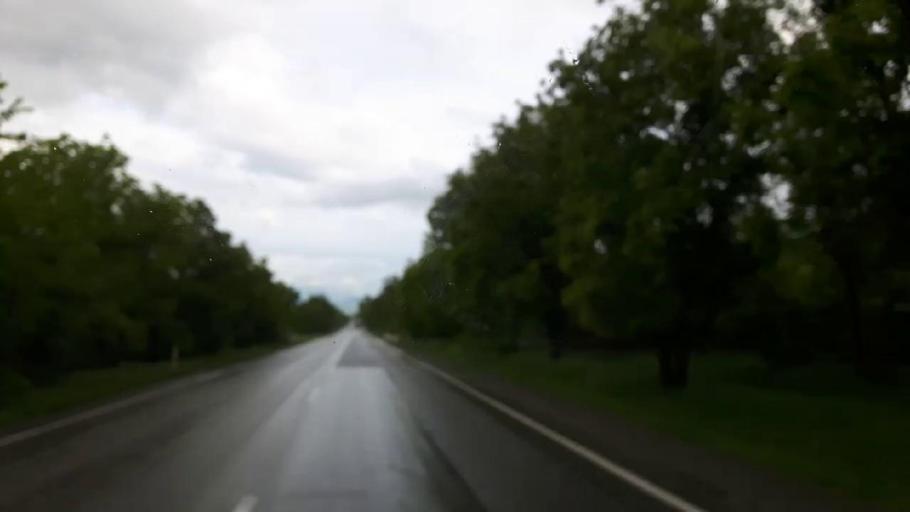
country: GE
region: Shida Kartli
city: Kaspi
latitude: 41.9706
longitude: 44.4540
